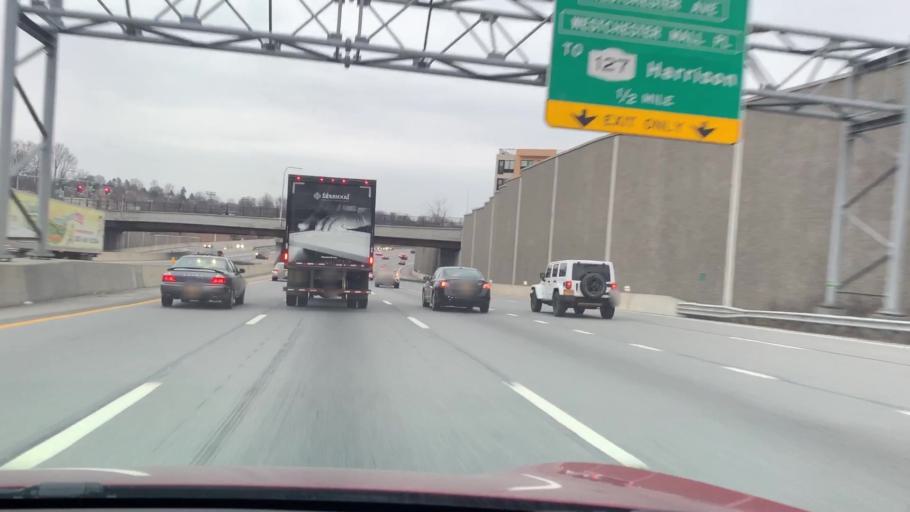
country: US
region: New York
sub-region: Westchester County
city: White Plains
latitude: 41.0391
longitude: -73.7596
